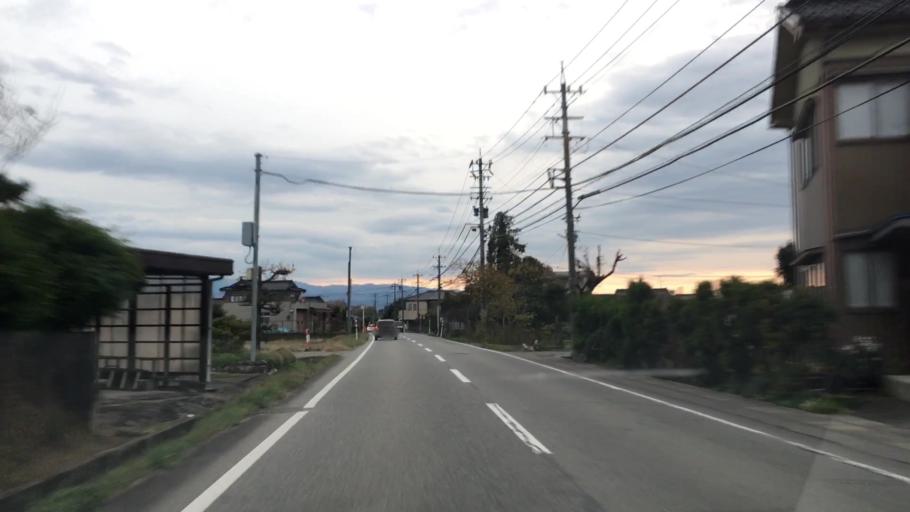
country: JP
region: Toyama
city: Kamiichi
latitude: 36.6976
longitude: 137.3150
